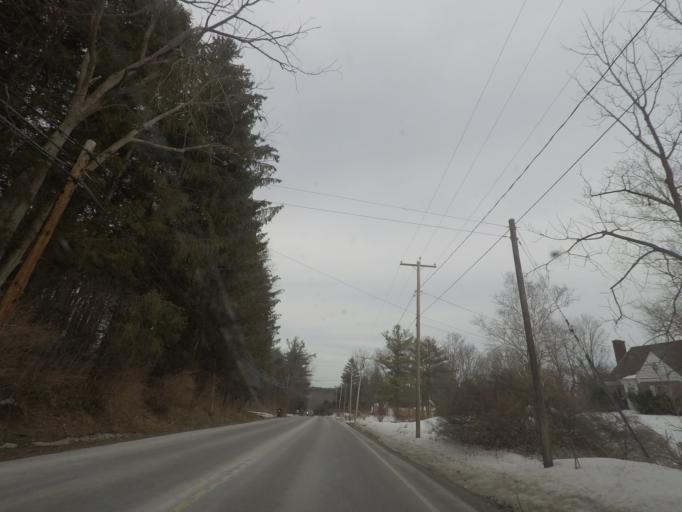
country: US
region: New York
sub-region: Albany County
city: Voorheesville
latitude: 42.5768
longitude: -73.9372
